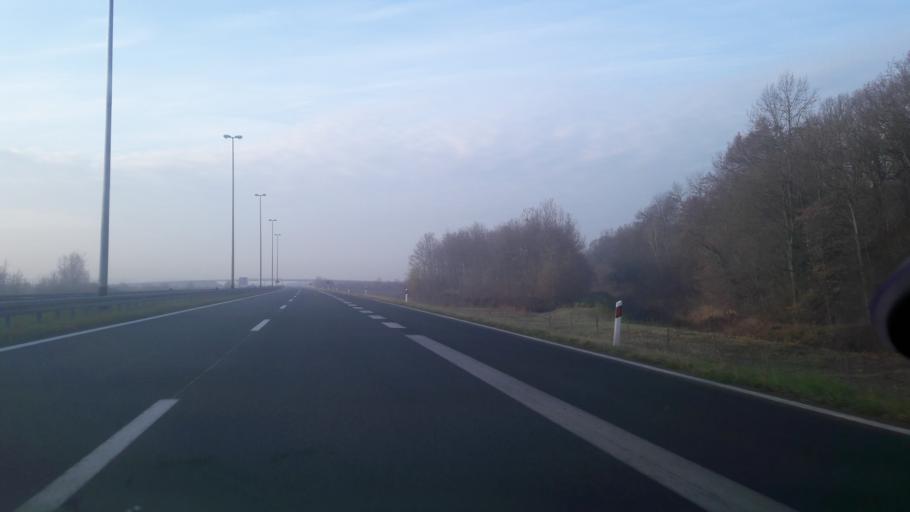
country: HR
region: Osjecko-Baranjska
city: Vuka
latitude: 45.4683
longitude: 18.4778
